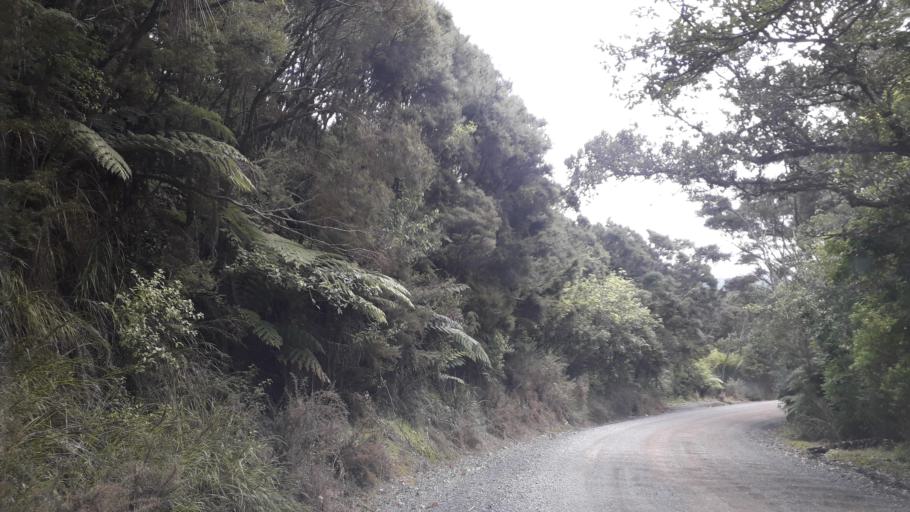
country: NZ
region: Northland
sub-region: Far North District
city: Paihia
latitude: -35.3170
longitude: 174.2273
